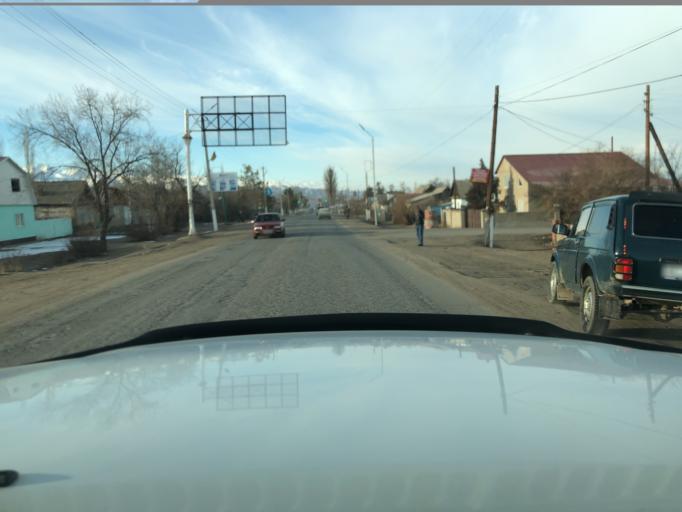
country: KG
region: Ysyk-Koel
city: Pokrovka
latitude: 42.3449
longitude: 78.0112
